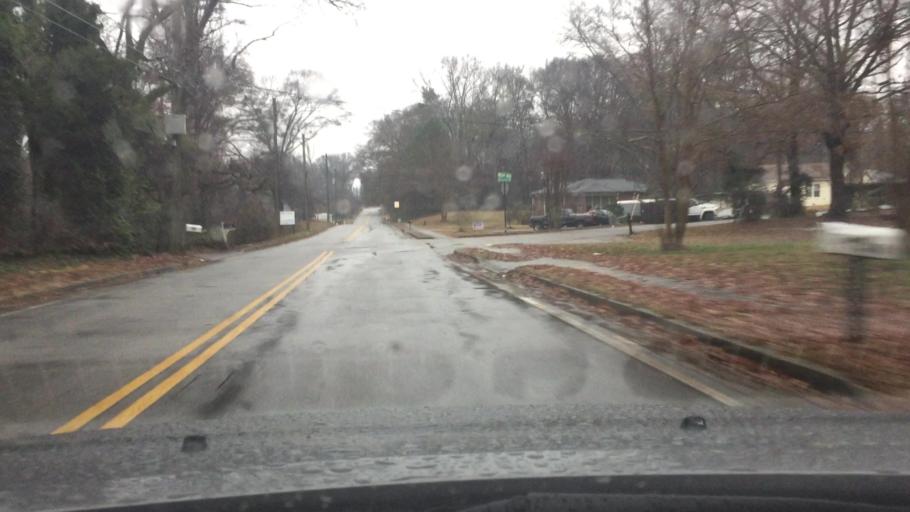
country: US
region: Georgia
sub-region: Cobb County
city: Fair Oaks
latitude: 33.9115
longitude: -84.5399
